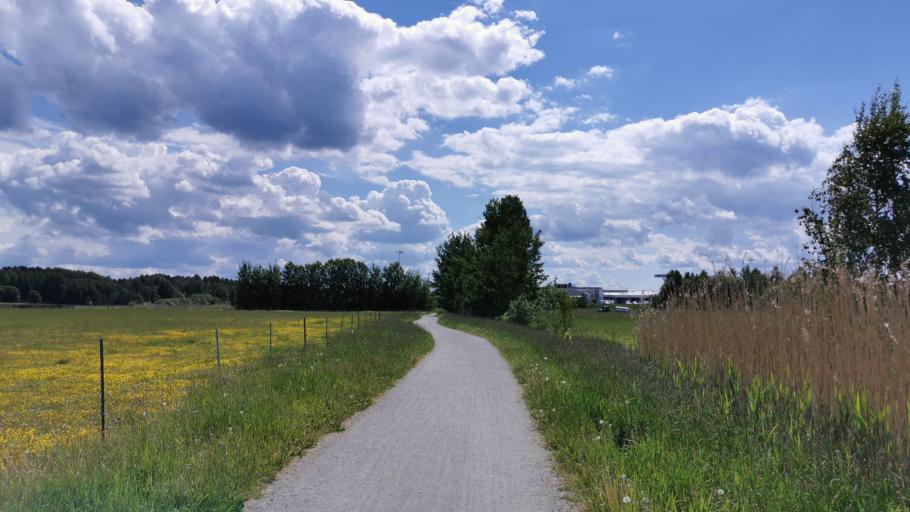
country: SE
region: OErebro
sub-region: Orebro Kommun
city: Orebro
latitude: 59.3013
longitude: 15.2087
